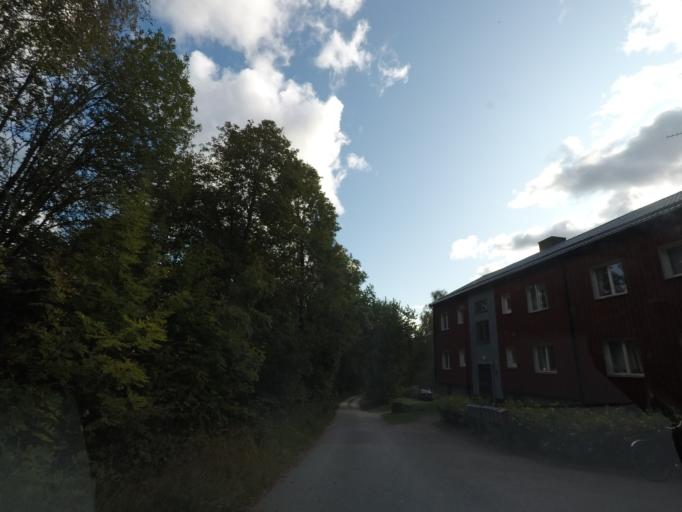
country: SE
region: Vaestmanland
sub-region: Skinnskattebergs Kommun
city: Skinnskatteberg
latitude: 59.8256
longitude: 15.6772
